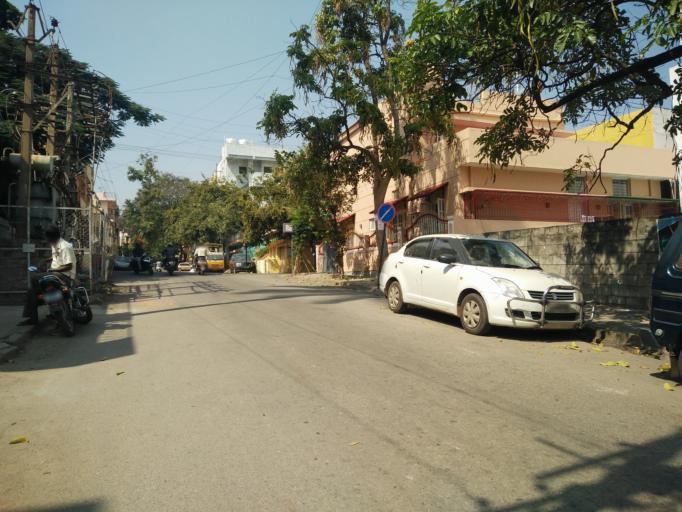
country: IN
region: Karnataka
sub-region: Bangalore Urban
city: Bangalore
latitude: 12.9726
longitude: 77.5459
